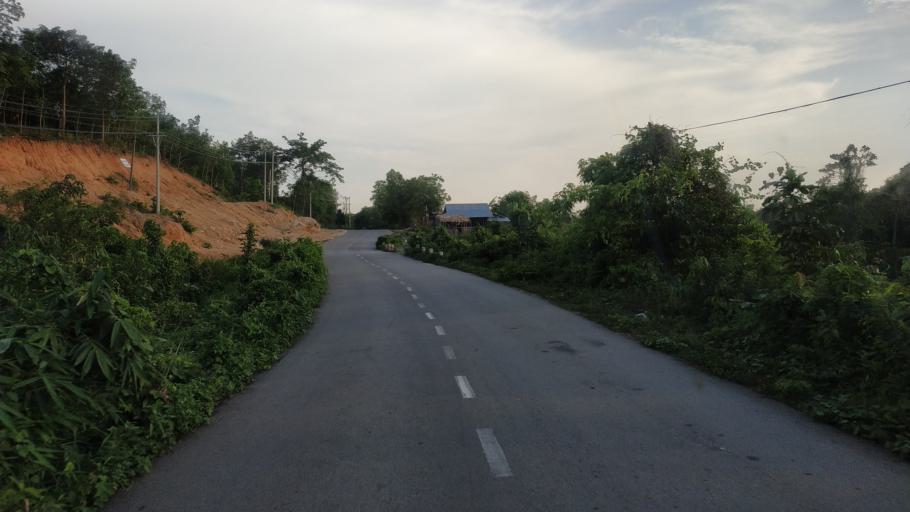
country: MM
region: Mon
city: Kyaikto
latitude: 17.4192
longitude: 97.0712
